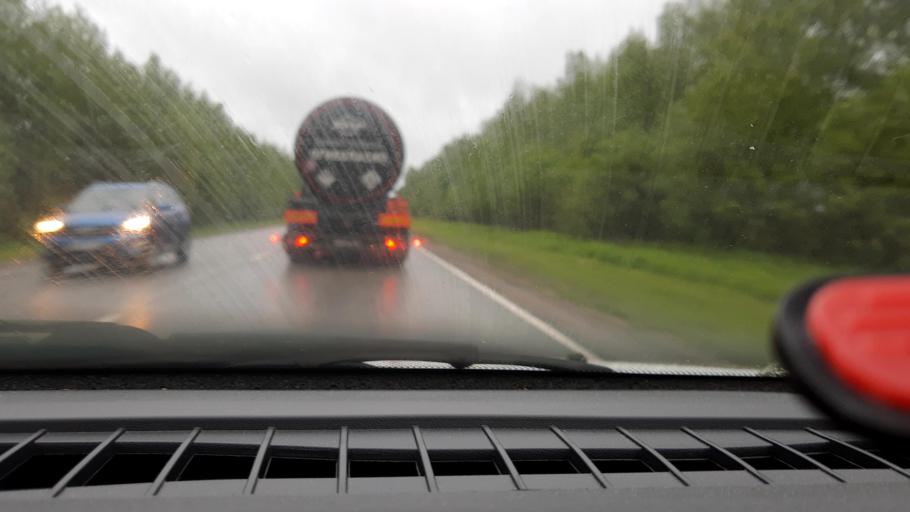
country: RU
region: Nizjnij Novgorod
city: Vladimirskoye
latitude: 56.9181
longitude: 45.0553
